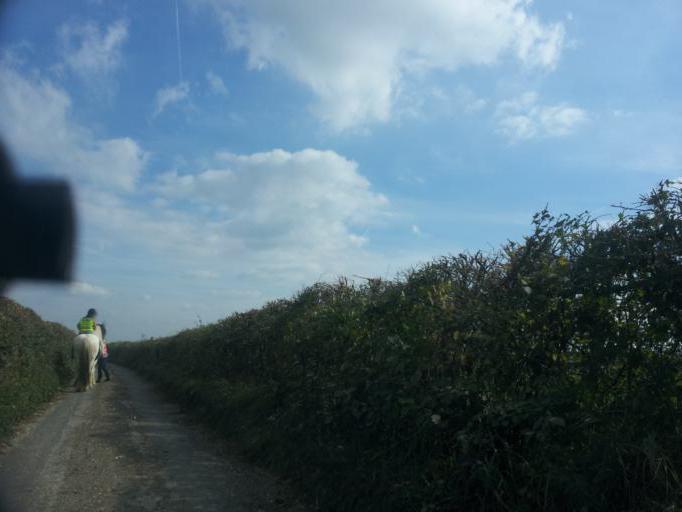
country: GB
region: England
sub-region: Kent
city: Boxley
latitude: 51.3218
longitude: 0.5277
